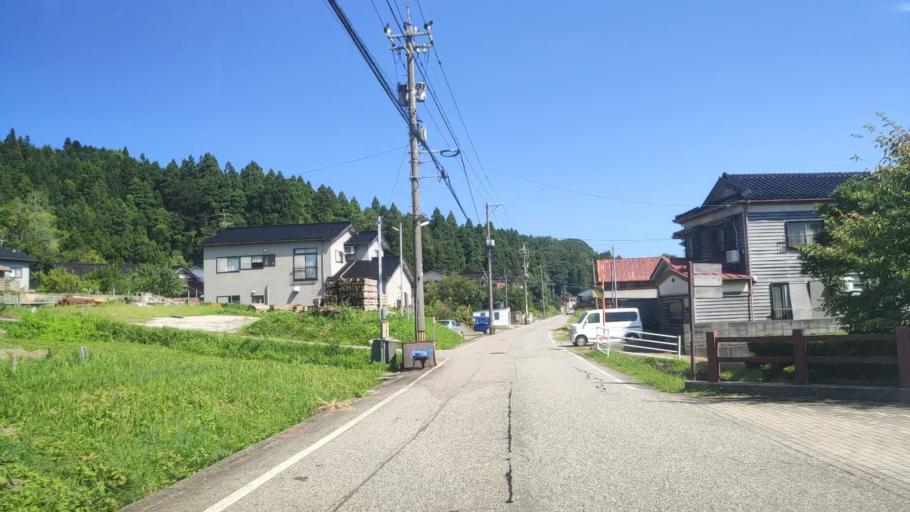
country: JP
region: Ishikawa
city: Nanao
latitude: 37.3800
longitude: 136.8807
